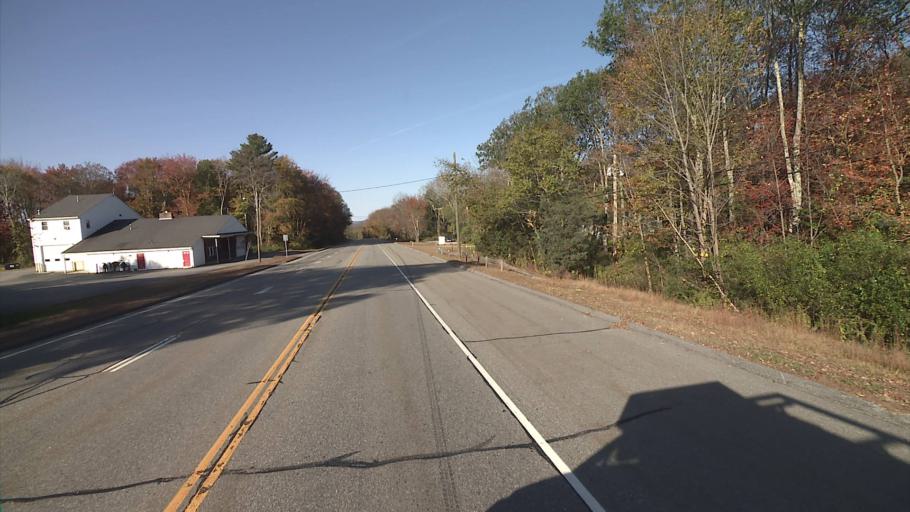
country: US
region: Connecticut
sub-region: Windham County
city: Danielson
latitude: 41.7909
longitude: -71.8223
